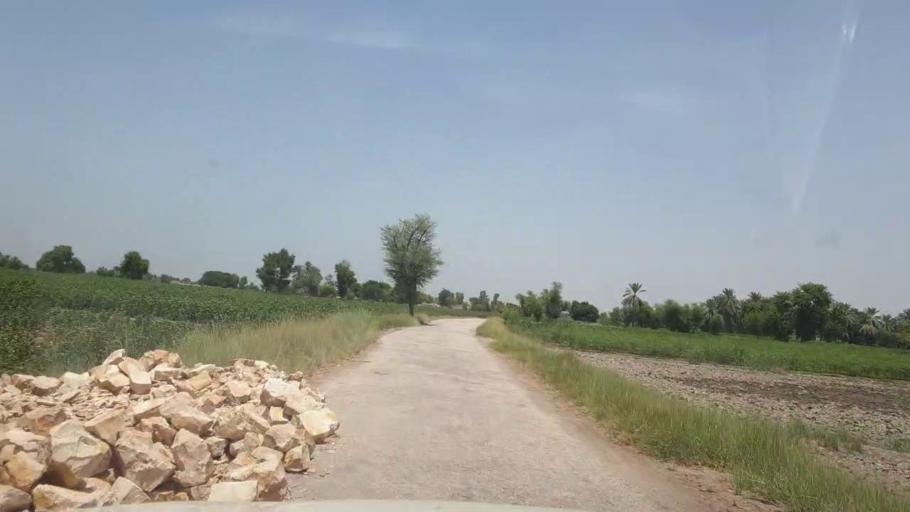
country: PK
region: Sindh
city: Bozdar
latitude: 27.1664
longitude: 68.6216
